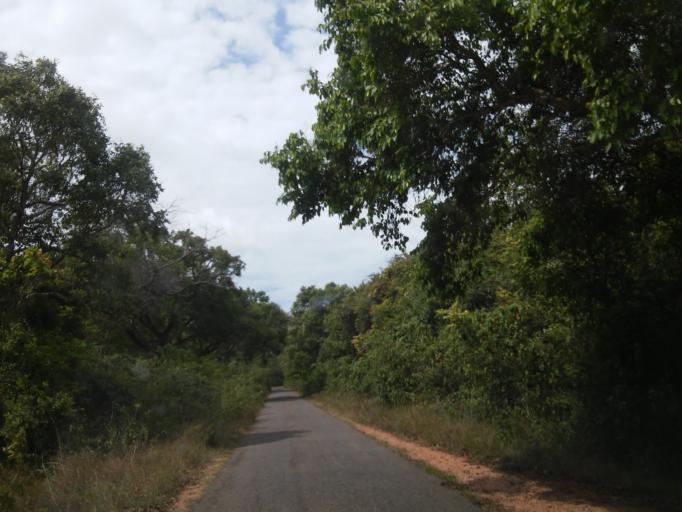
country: LK
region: Central
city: Sigiriya
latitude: 8.0998
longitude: 80.6808
